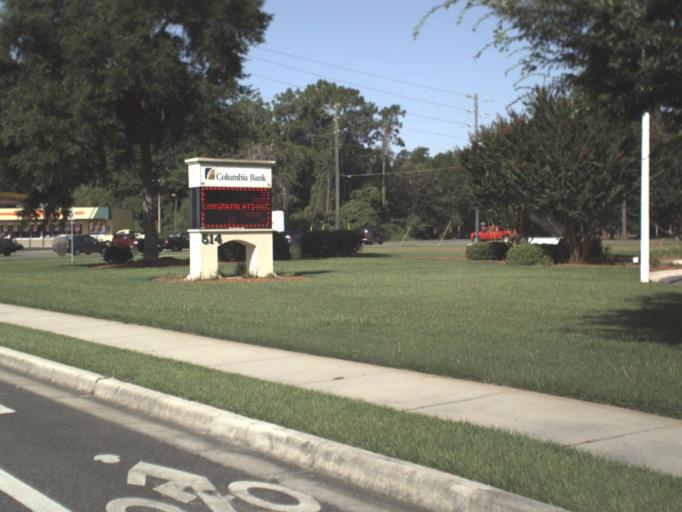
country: US
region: Florida
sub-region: Columbia County
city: Lake City
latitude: 30.1645
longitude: -82.6438
